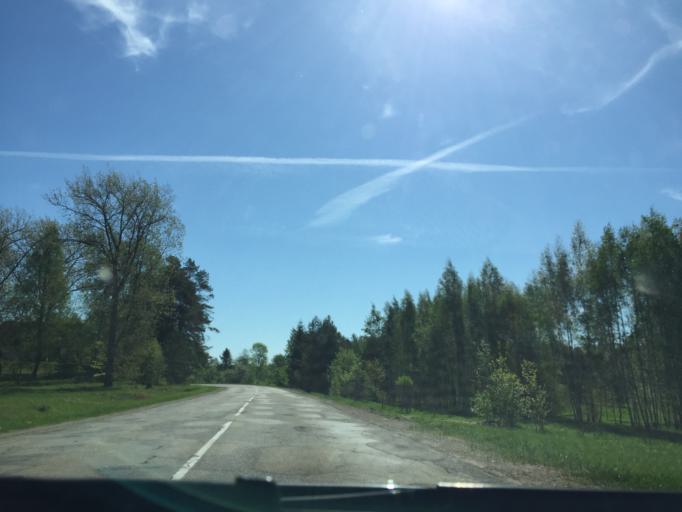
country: LV
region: Ropazu
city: Ropazi
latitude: 57.0071
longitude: 24.5726
